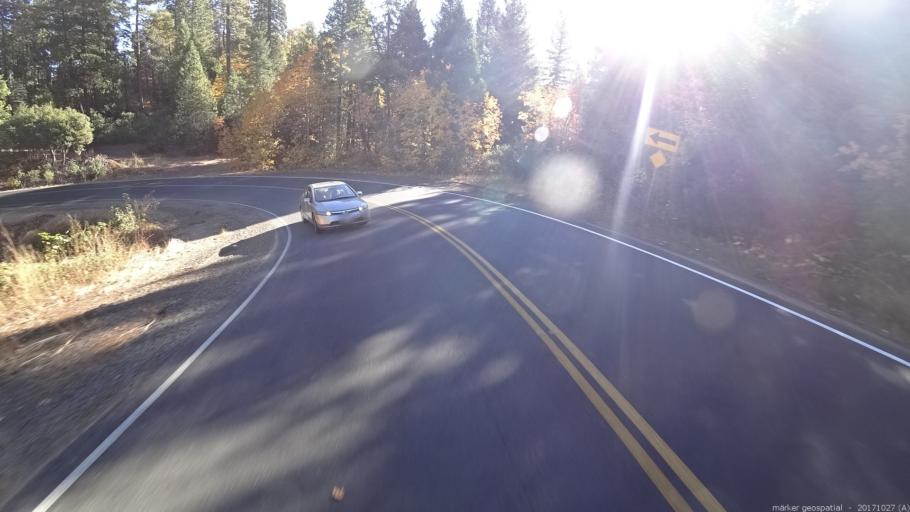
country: US
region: California
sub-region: Shasta County
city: Burney
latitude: 40.8865
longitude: -121.9068
